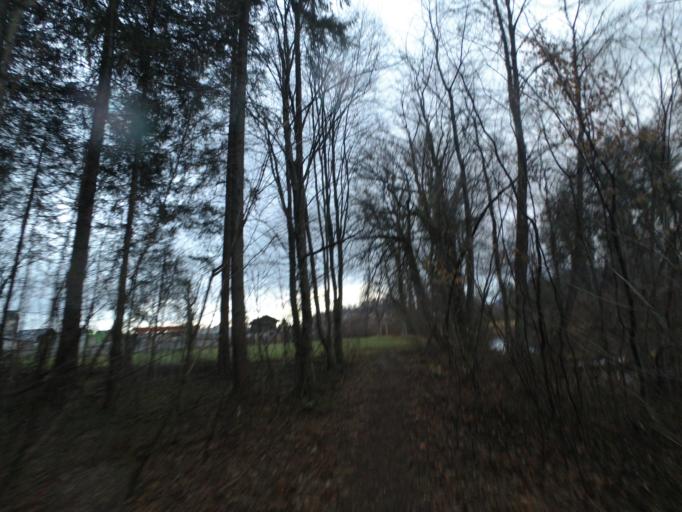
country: AT
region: Salzburg
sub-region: Politischer Bezirk Salzburg-Umgebung
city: Anif
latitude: 47.7471
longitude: 13.0693
